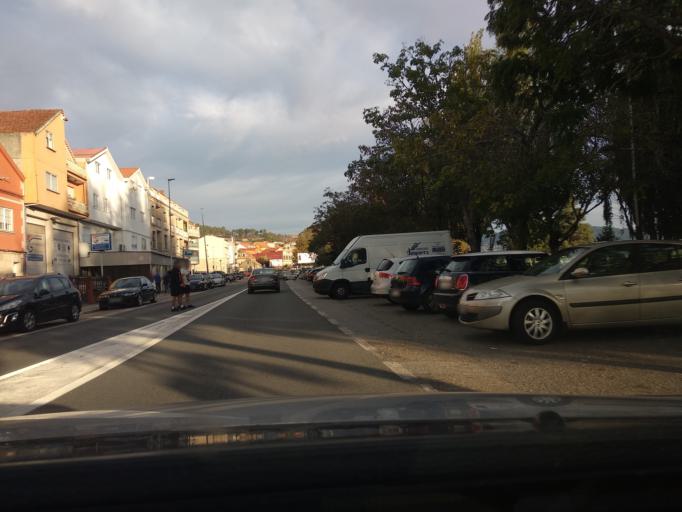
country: ES
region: Galicia
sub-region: Provincia de Pontevedra
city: Moana
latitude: 42.2873
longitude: -8.7268
